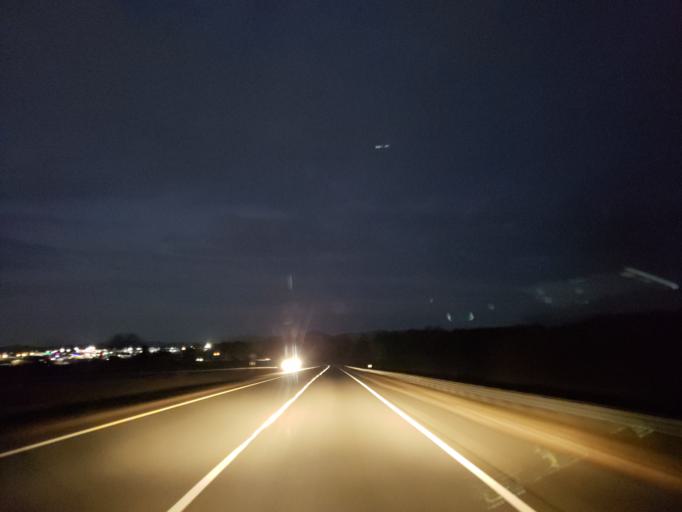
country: US
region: Georgia
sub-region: Polk County
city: Rockmart
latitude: 34.0010
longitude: -85.0256
